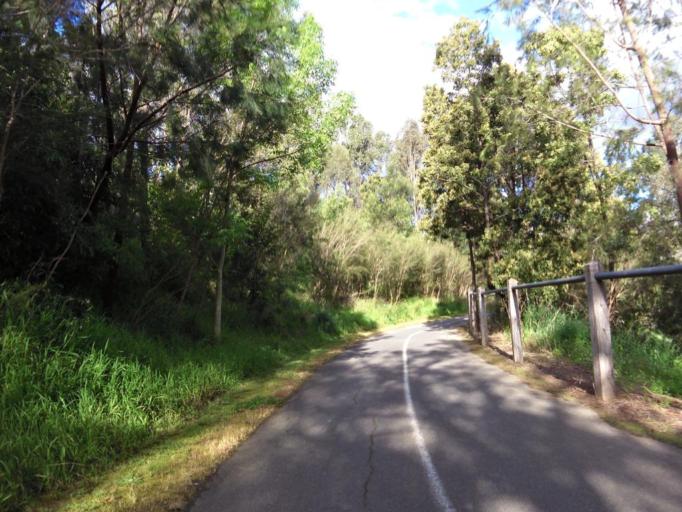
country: AU
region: Victoria
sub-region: Manningham
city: Doncaster East
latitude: -37.7968
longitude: 145.1413
